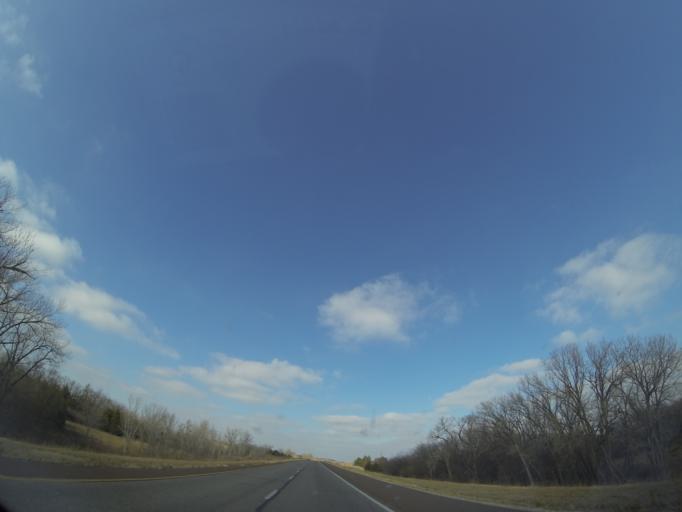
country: US
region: Kansas
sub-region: McPherson County
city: Lindsborg
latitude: 38.4903
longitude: -97.6190
